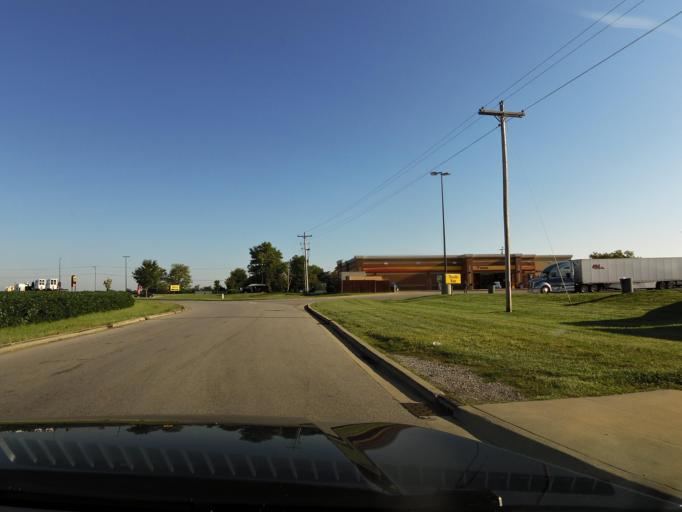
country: US
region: Illinois
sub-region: Clinton County
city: New Baden
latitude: 38.5336
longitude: -89.7330
